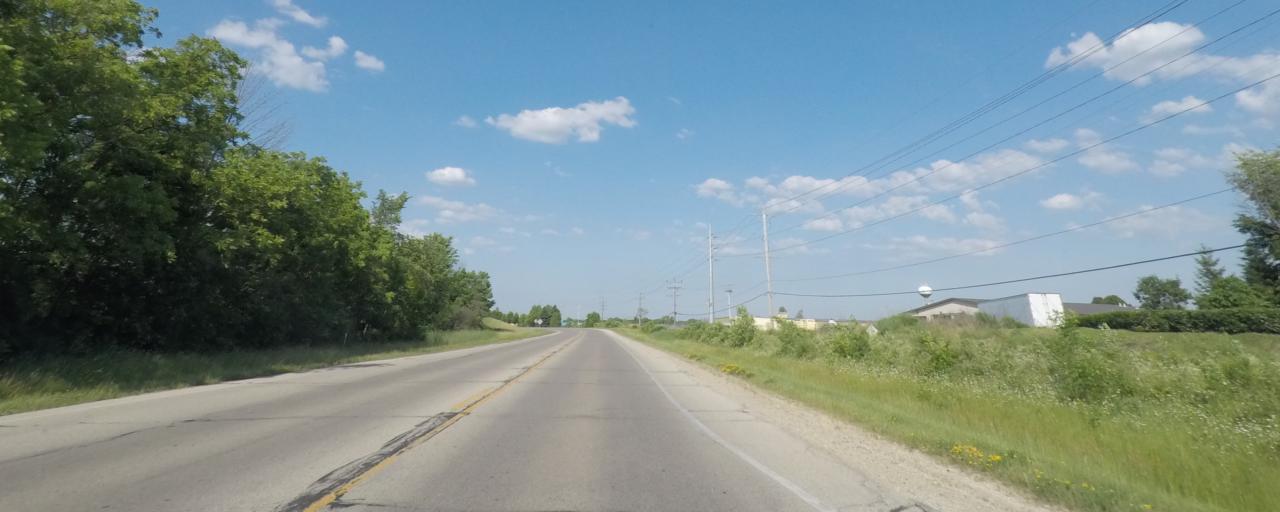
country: US
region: Wisconsin
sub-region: Waukesha County
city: Muskego
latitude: 42.8950
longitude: -88.1596
